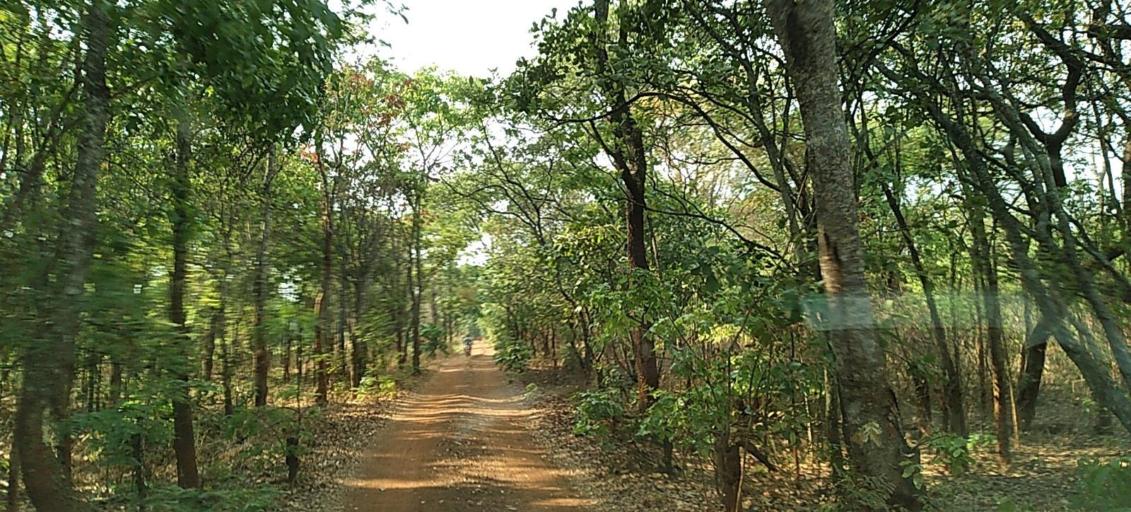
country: ZM
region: Copperbelt
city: Kalulushi
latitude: -12.9690
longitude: 27.7139
